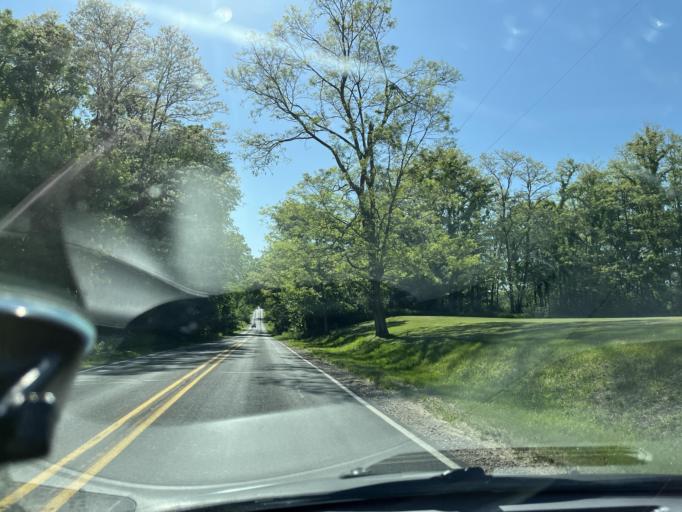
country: US
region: Michigan
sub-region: Barry County
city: Hastings
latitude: 42.6530
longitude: -85.3371
